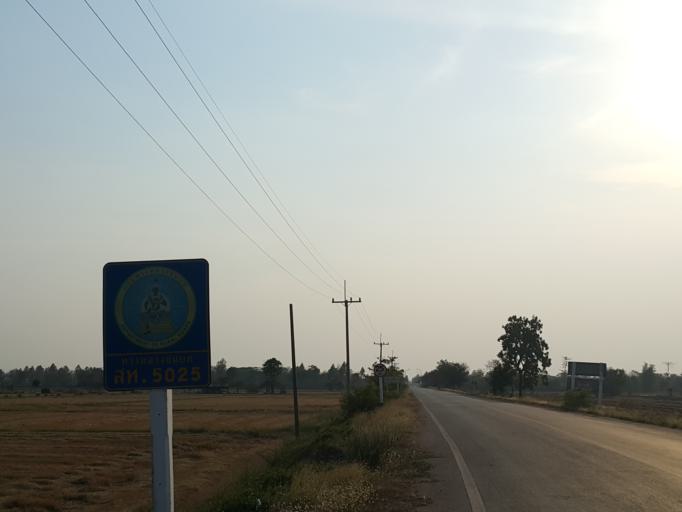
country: TH
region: Sukhothai
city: Si Samrong
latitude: 17.2267
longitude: 99.9532
